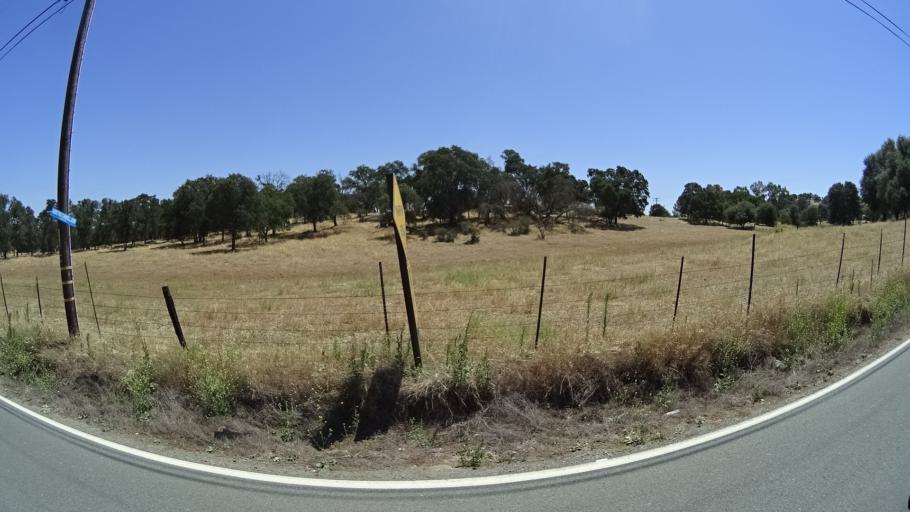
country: US
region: California
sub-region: Calaveras County
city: Rancho Calaveras
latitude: 38.1348
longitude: -120.9134
